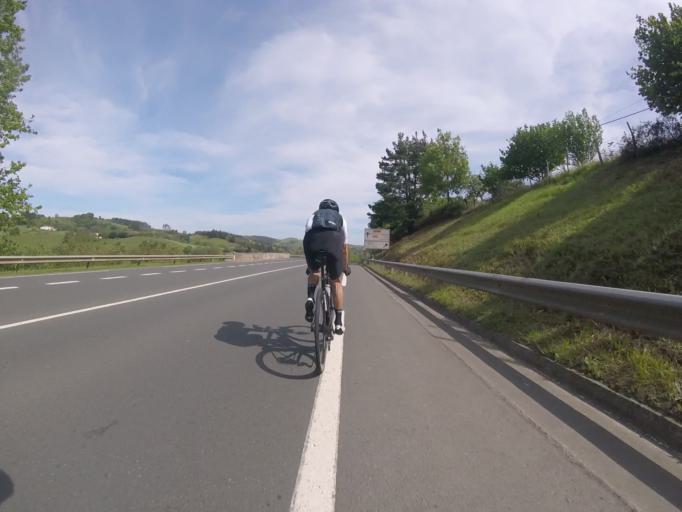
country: ES
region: Basque Country
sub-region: Provincia de Guipuzcoa
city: Cestona
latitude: 43.2615
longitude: -2.2715
